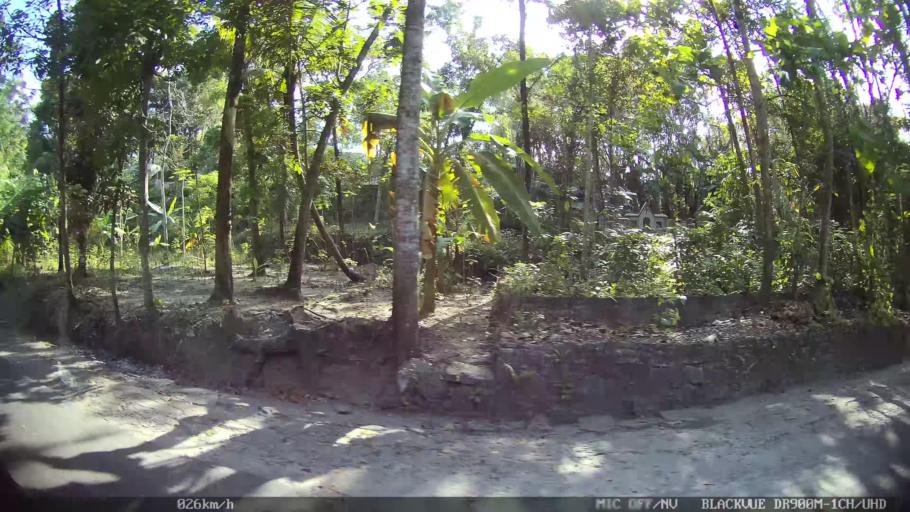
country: ID
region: Daerah Istimewa Yogyakarta
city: Kasihan
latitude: -7.8345
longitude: 110.3367
